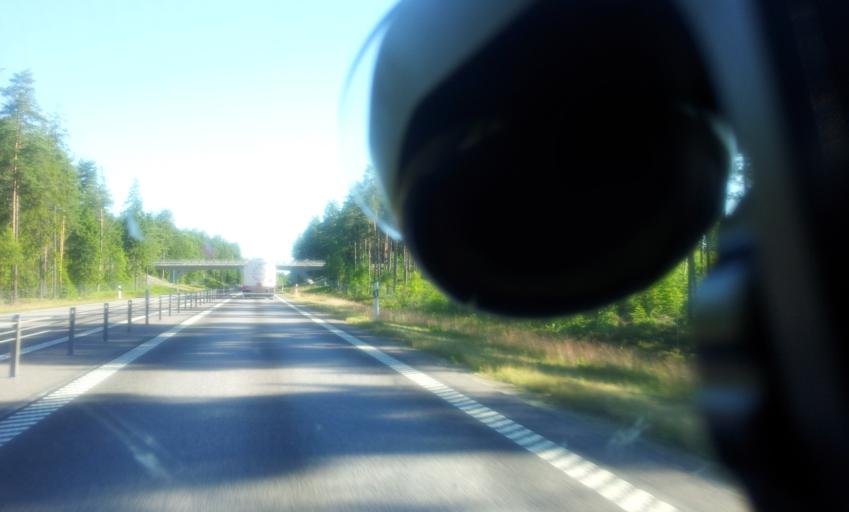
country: SE
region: Kalmar
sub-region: Kalmar Kommun
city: Ljungbyholm
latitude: 56.5314
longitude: 16.0841
